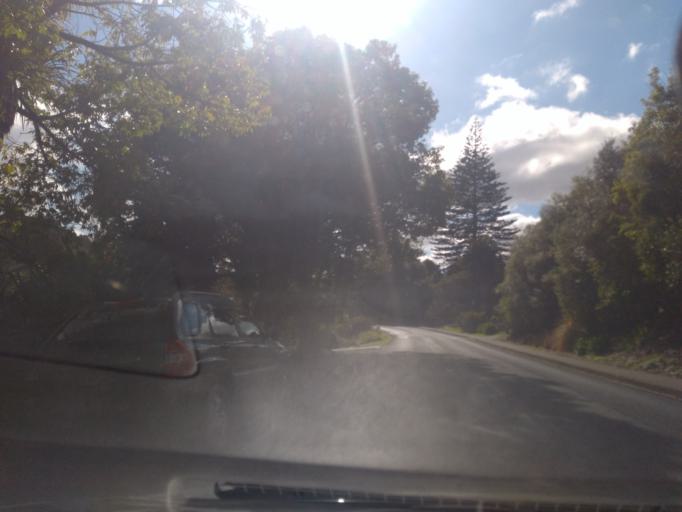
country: NZ
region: Northland
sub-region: Whangarei
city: Whangarei
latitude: -35.7015
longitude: 174.3314
